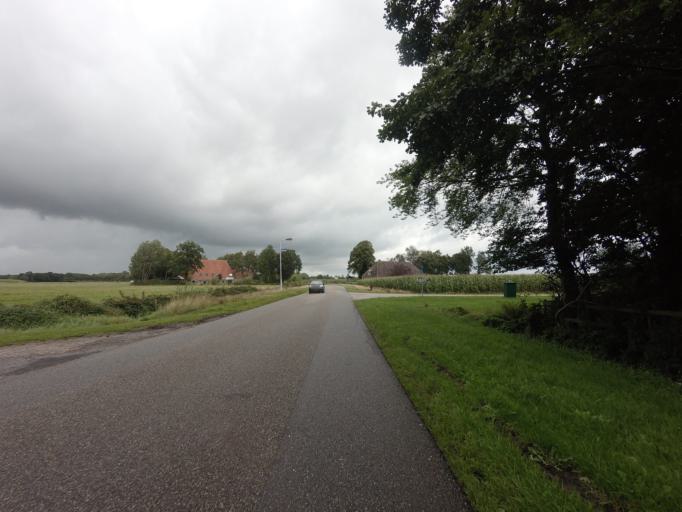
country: NL
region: Drenthe
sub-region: Gemeente Westerveld
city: Dwingeloo
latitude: 52.9740
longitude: 6.2925
